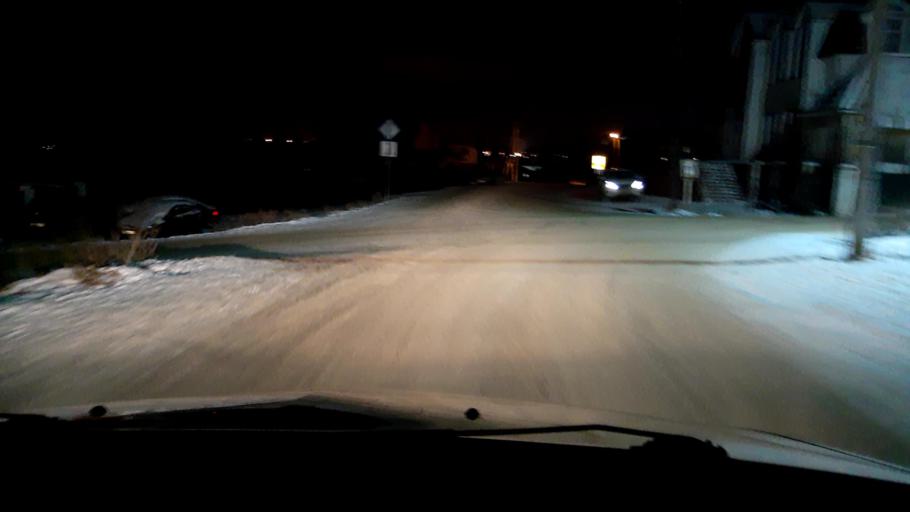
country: RU
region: Bashkortostan
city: Mikhaylovka
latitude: 54.8091
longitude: 55.8952
